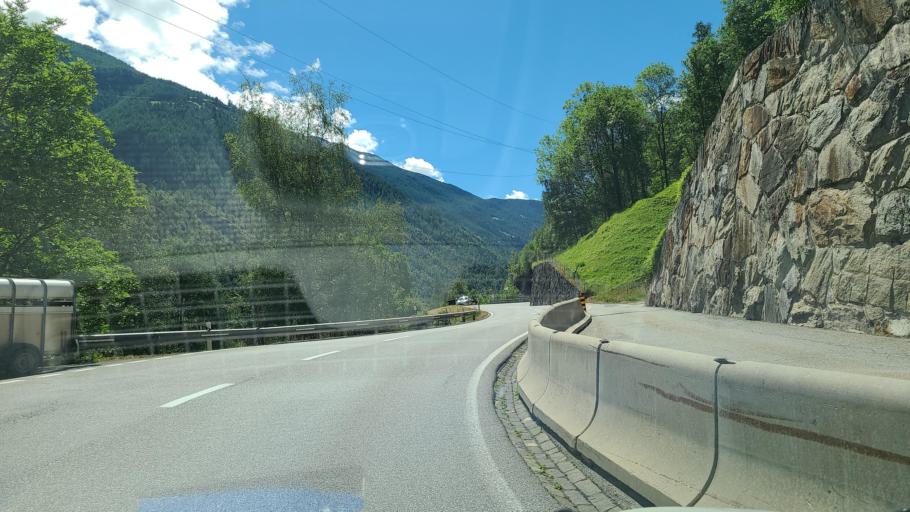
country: CH
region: Valais
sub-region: Visp District
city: Stalden
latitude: 46.2216
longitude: 7.8762
